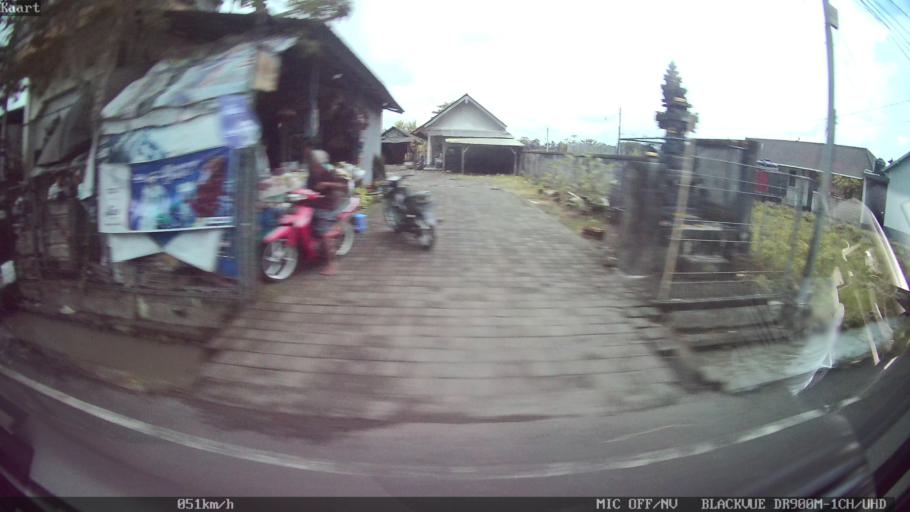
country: ID
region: Bali
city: Banjar Serangan
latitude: -8.5548
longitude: 115.1804
